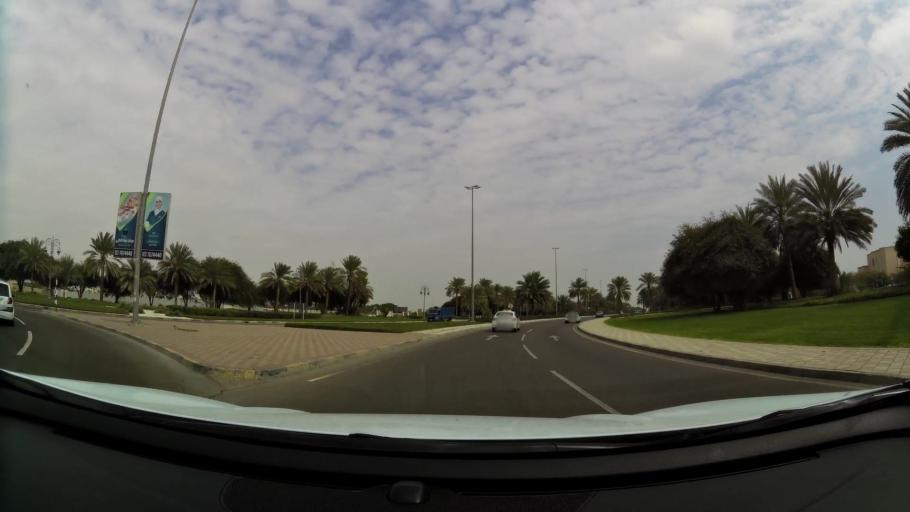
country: AE
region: Abu Dhabi
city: Al Ain
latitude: 24.2058
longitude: 55.7886
